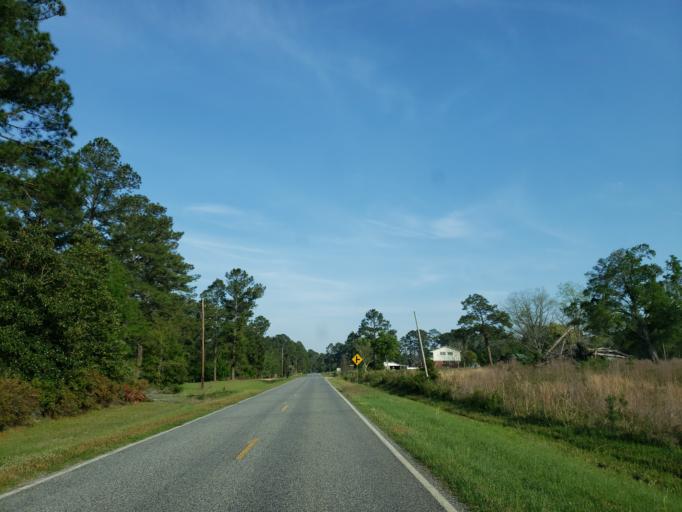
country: US
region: Georgia
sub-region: Tift County
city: Tifton
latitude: 31.4968
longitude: -83.5526
